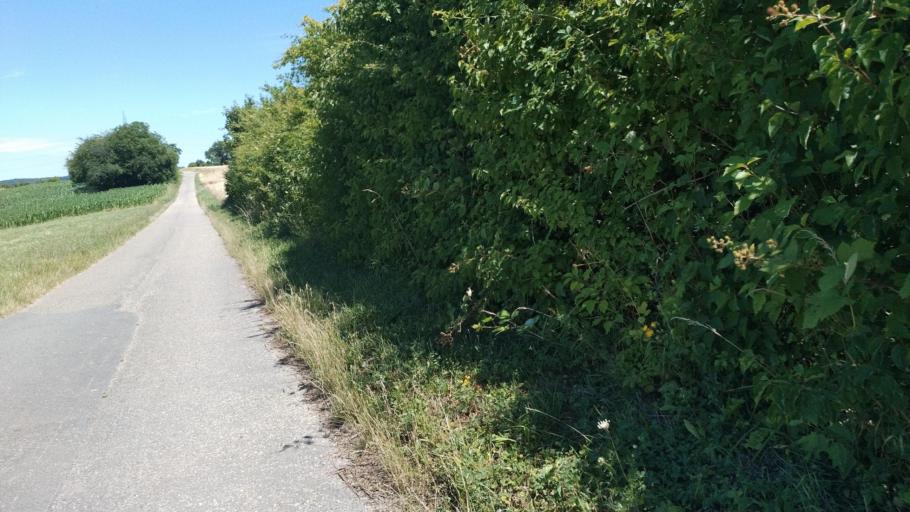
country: DE
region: Baden-Wuerttemberg
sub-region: Karlsruhe Region
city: Ubstadt-Weiher
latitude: 49.1442
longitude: 8.6168
